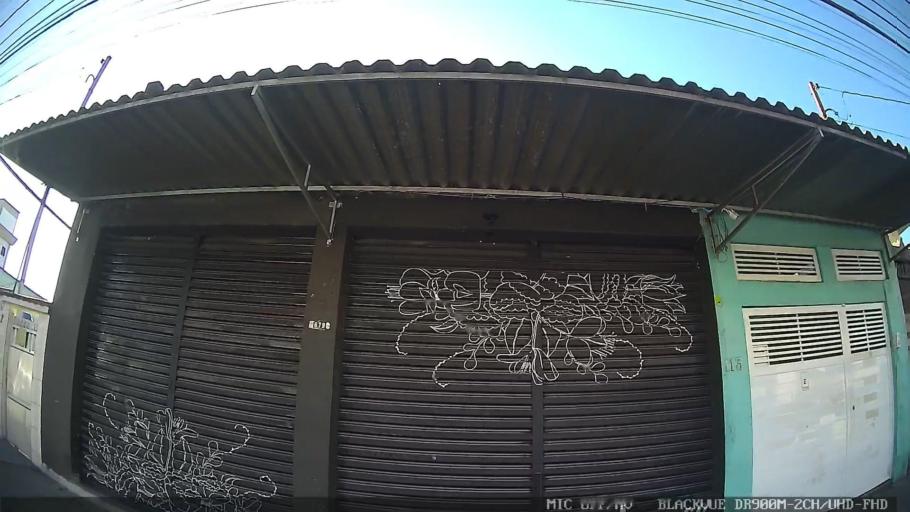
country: BR
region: Sao Paulo
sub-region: Santos
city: Santos
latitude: -23.9600
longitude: -46.2939
